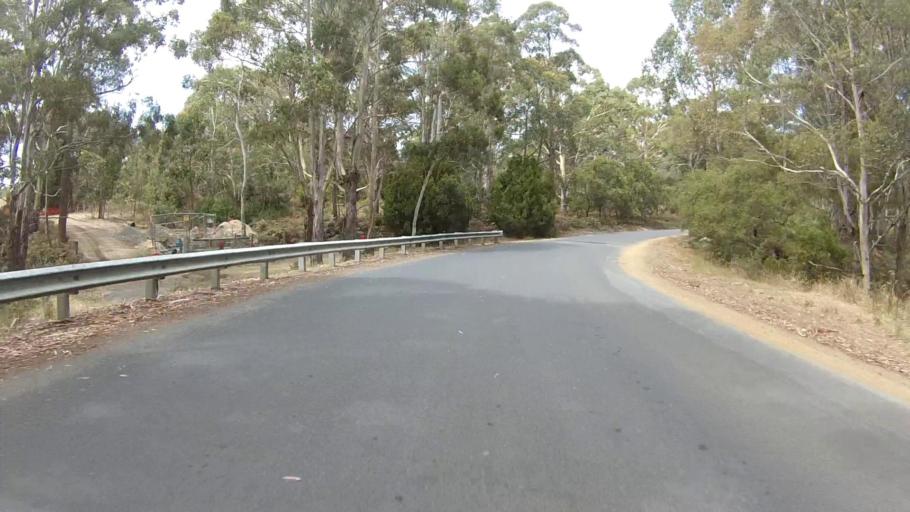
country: AU
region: Tasmania
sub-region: Kingborough
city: Margate
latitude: -43.0083
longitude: 147.2848
